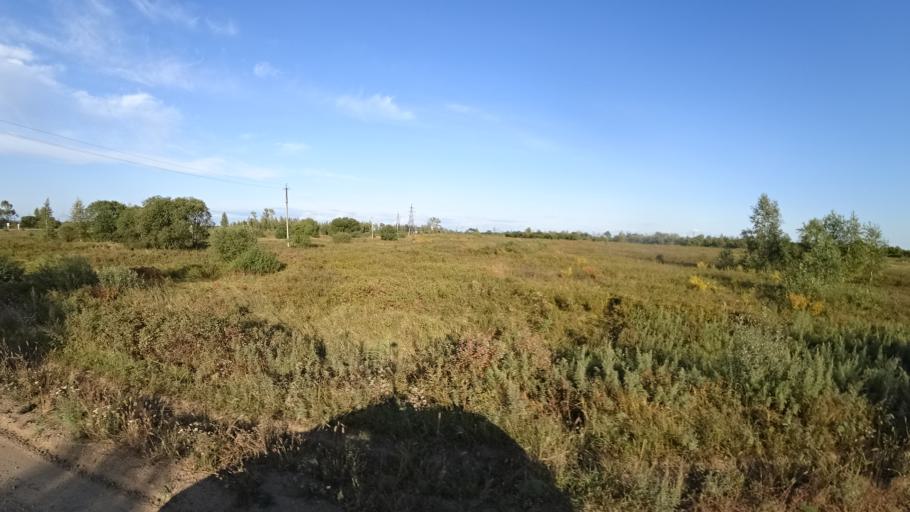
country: RU
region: Amur
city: Arkhara
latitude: 49.3679
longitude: 130.1359
